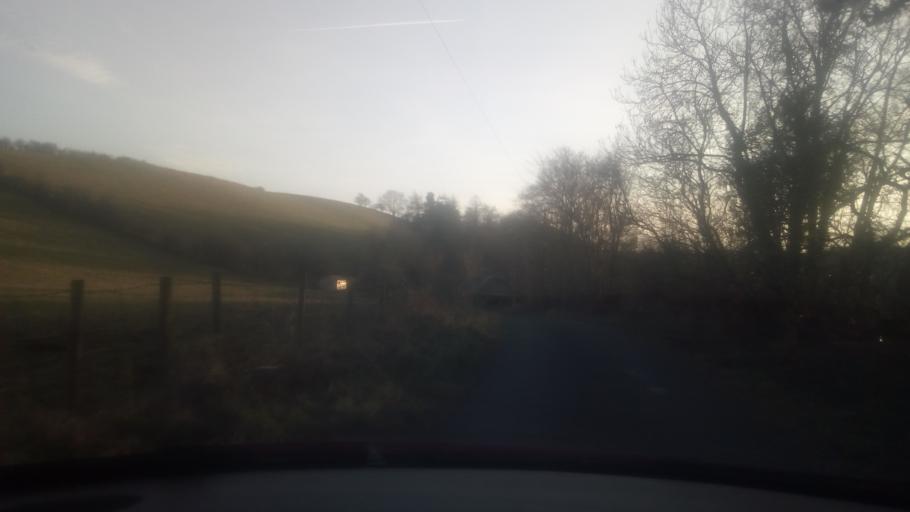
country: GB
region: Scotland
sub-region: The Scottish Borders
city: Jedburgh
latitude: 55.4982
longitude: -2.5410
